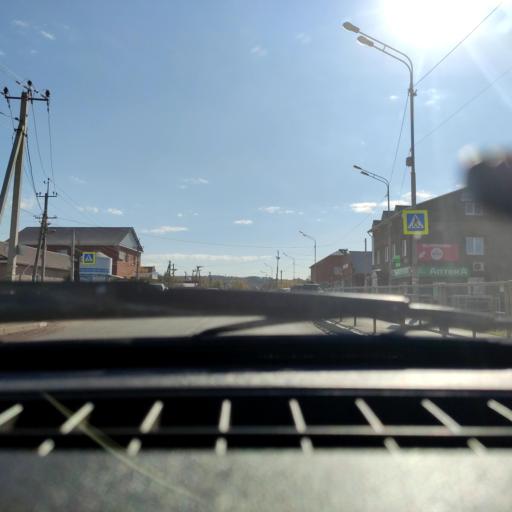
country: RU
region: Bashkortostan
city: Ufa
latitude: 54.6136
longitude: 55.9364
